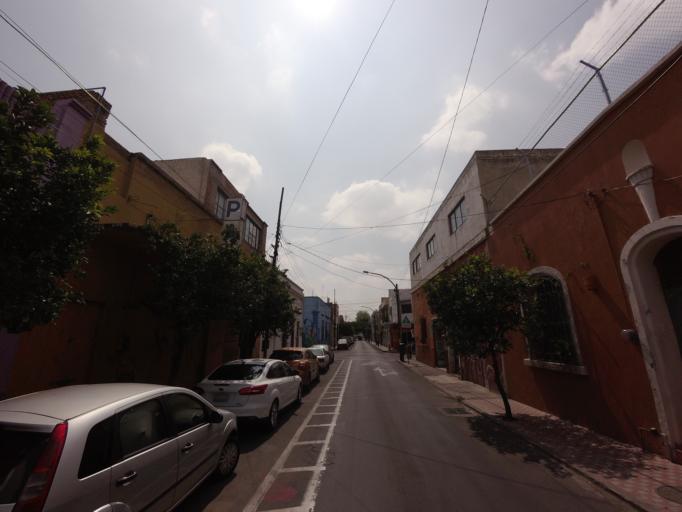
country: MX
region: Jalisco
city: Guadalajara
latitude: 20.6787
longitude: -103.3567
